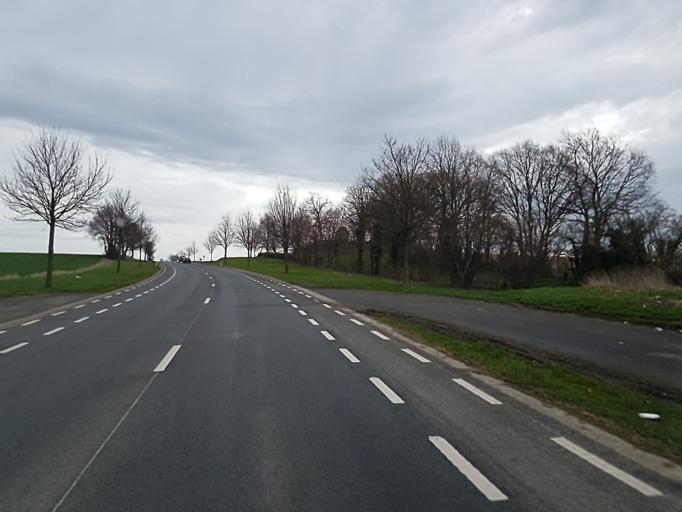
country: BE
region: Wallonia
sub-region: Province de Liege
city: Oreye
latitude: 50.7367
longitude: 5.3659
